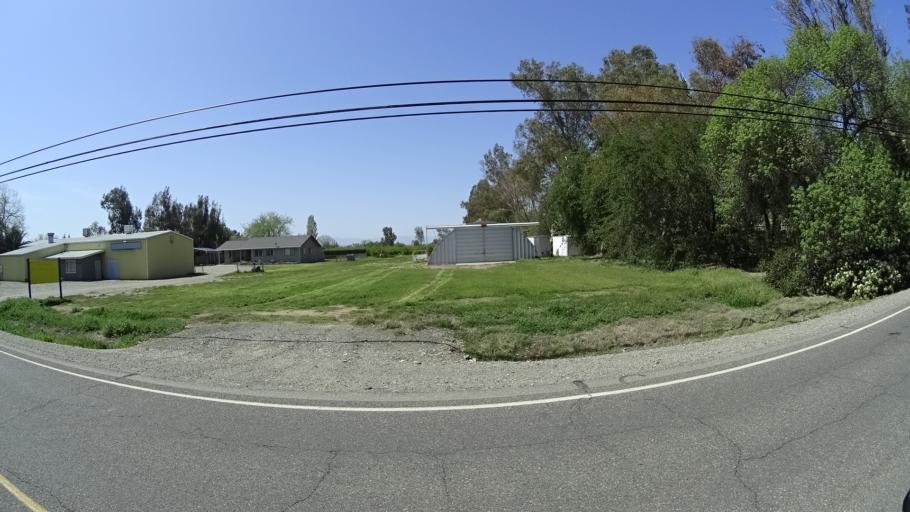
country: US
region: California
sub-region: Glenn County
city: Orland
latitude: 39.7166
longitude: -122.1970
